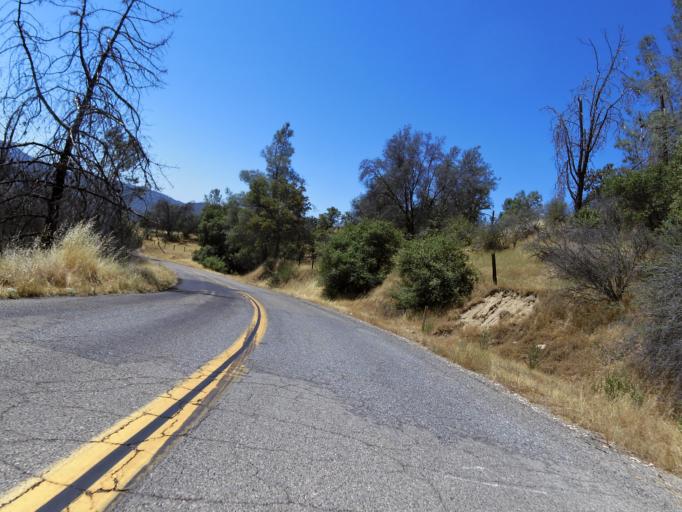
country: US
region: California
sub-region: Fresno County
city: Auberry
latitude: 37.1698
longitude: -119.5151
